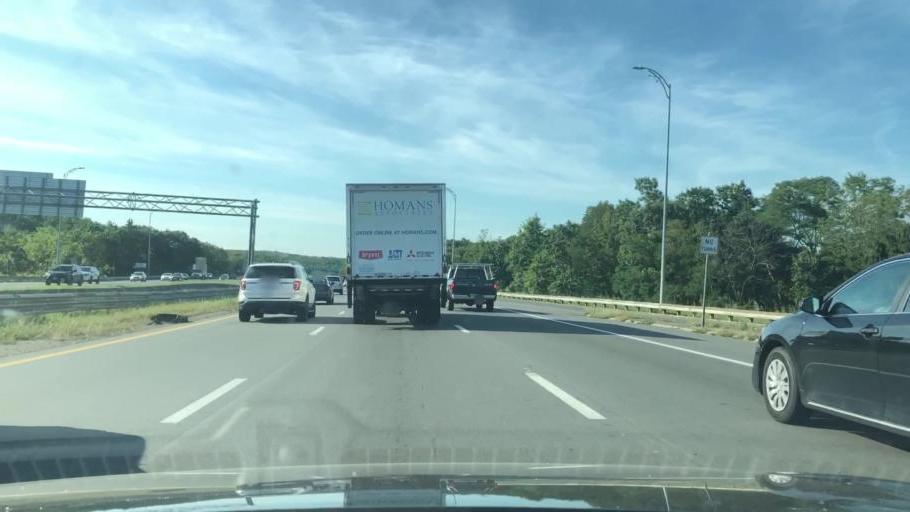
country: US
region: Massachusetts
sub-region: Essex County
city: North Andover
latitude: 42.6954
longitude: -71.1445
